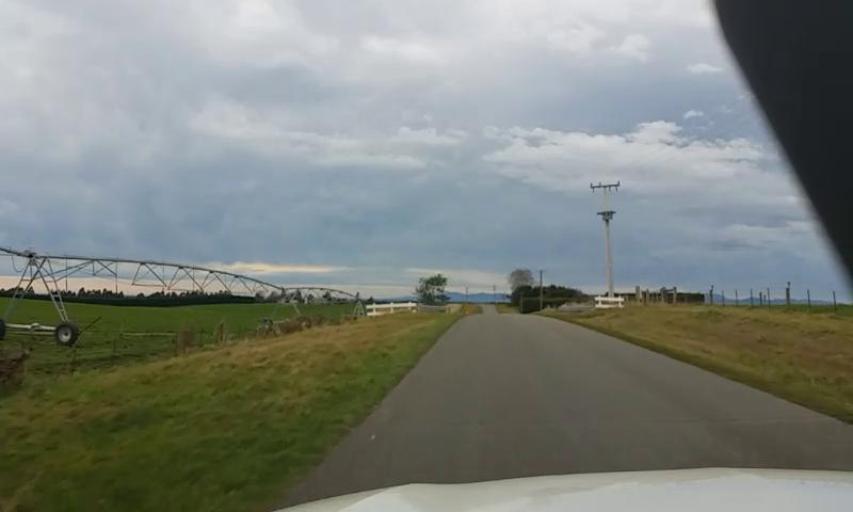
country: NZ
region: Canterbury
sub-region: Waimakariri District
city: Kaiapoi
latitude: -43.2946
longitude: 172.4740
